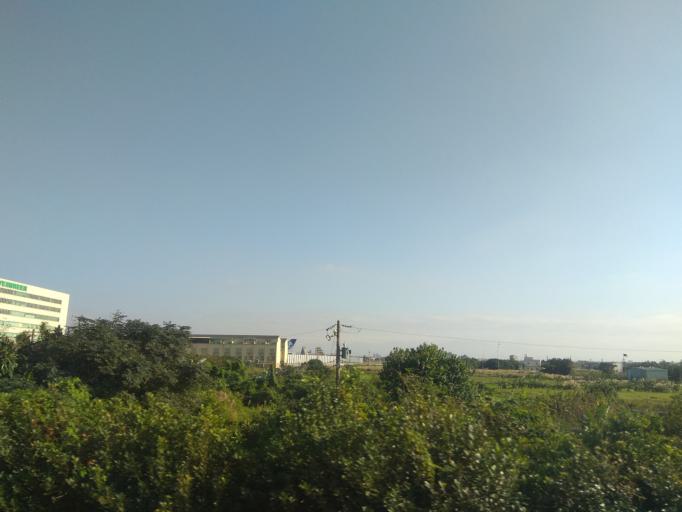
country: TW
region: Taiwan
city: Taoyuan City
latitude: 25.0650
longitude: 121.2169
